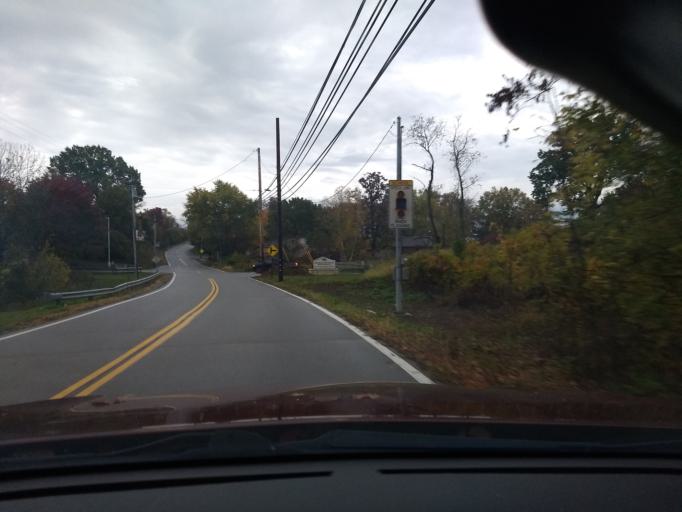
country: US
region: Pennsylvania
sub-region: Allegheny County
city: Jefferson Hills
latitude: 40.2978
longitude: -79.9359
